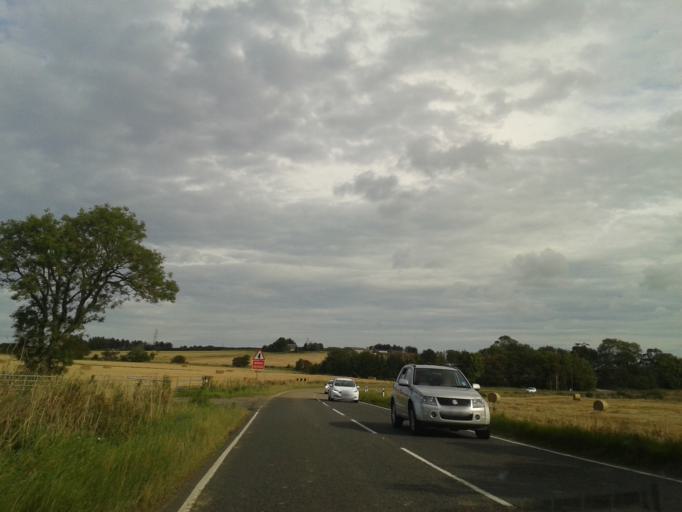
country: GB
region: Scotland
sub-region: Aberdeenshire
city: Whitehills
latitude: 57.6530
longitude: -2.6272
